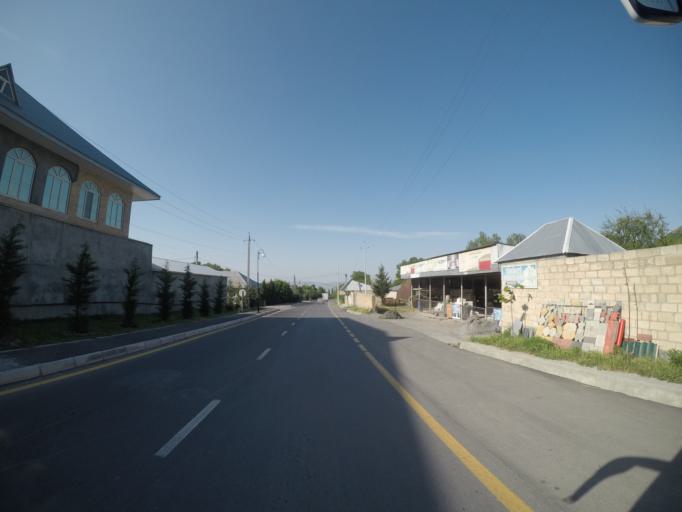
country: AZ
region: Shaki City
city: Sheki
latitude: 41.2164
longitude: 47.1686
